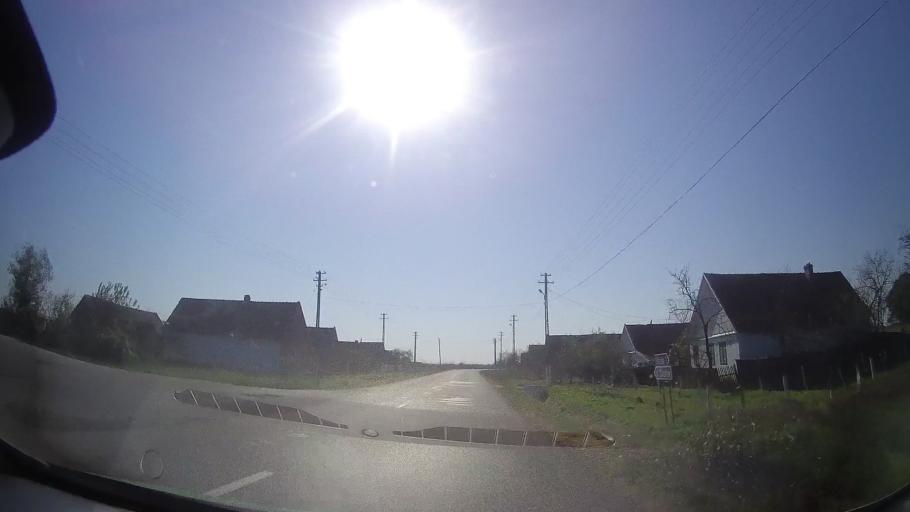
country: RO
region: Timis
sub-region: Comuna Ghizela
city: Ghizela
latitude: 45.7908
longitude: 21.7299
